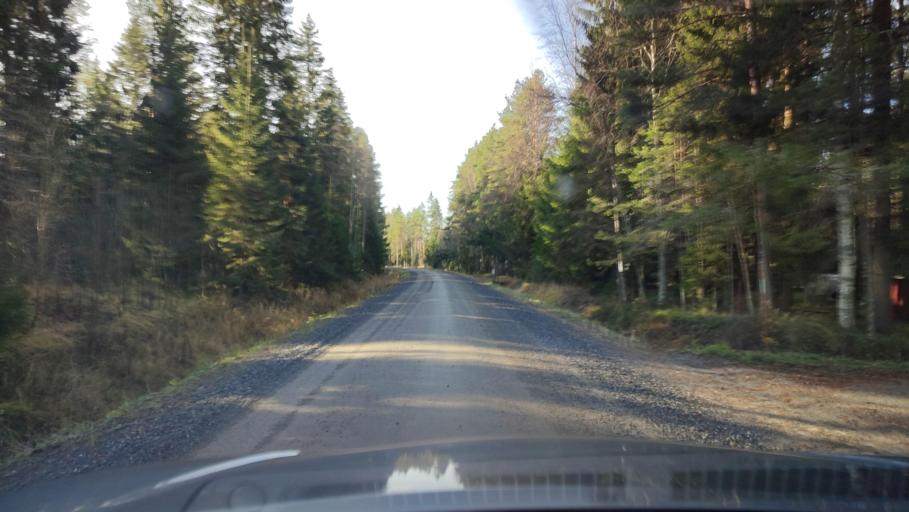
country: FI
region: Southern Ostrobothnia
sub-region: Suupohja
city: Teuva
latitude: 62.4543
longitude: 21.6184
